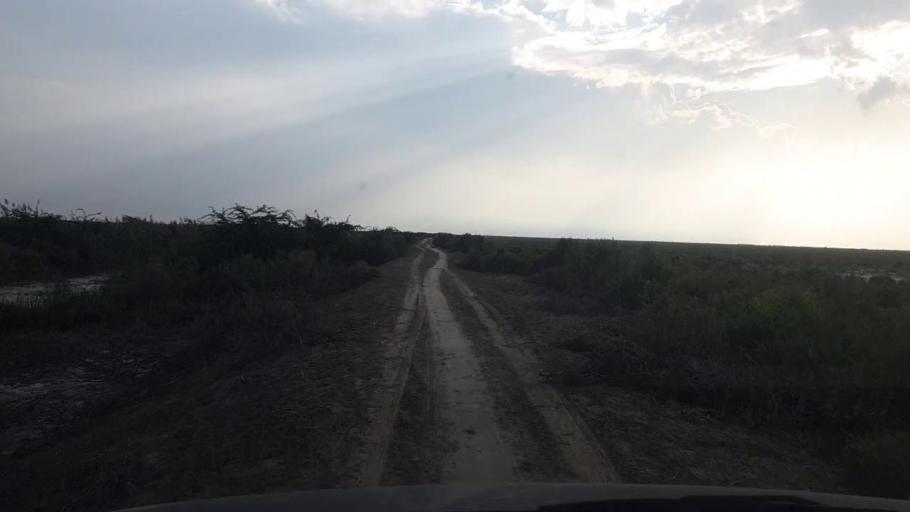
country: PK
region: Sindh
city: Badin
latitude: 24.4435
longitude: 68.6778
